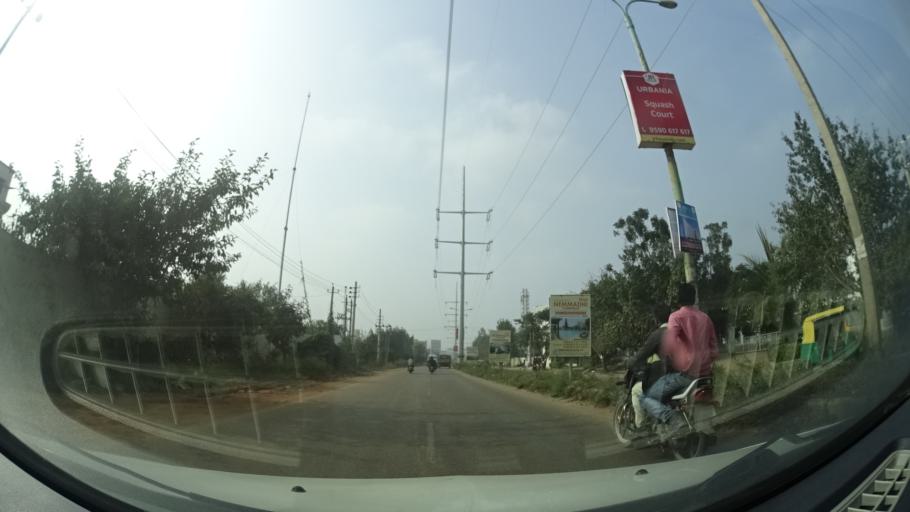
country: IN
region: Karnataka
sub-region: Bangalore Urban
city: Anekal
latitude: 12.7946
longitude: 77.6595
